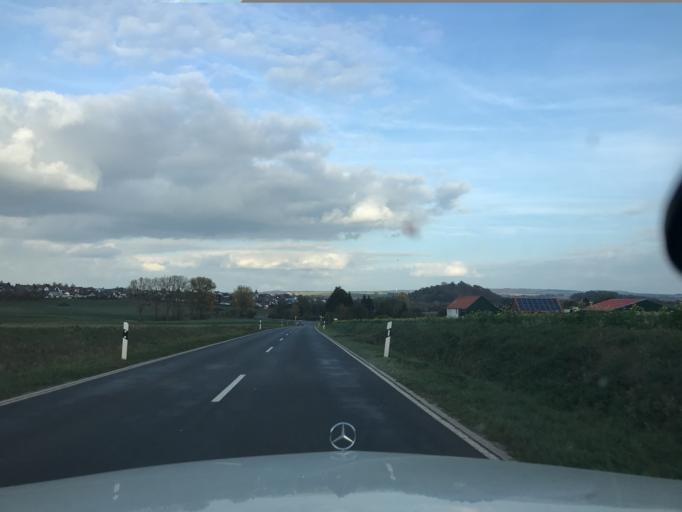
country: DE
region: Hesse
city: Grebenstein
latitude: 51.4377
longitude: 9.3917
